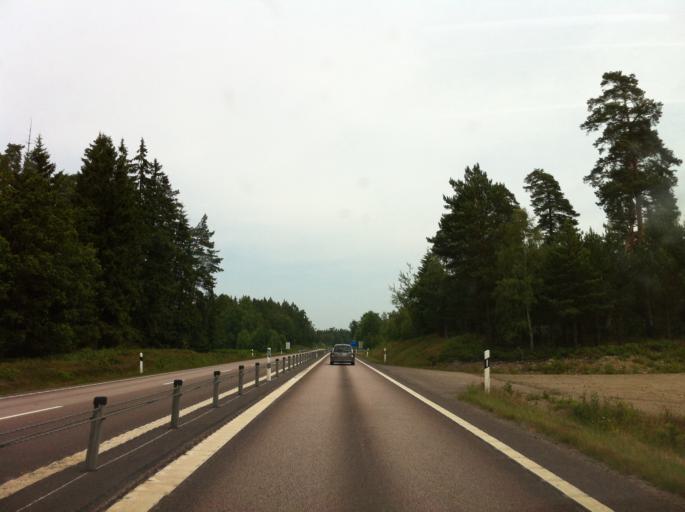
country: SE
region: Kalmar
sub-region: Torsas Kommun
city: Torsas
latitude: 56.2824
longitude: 15.9794
